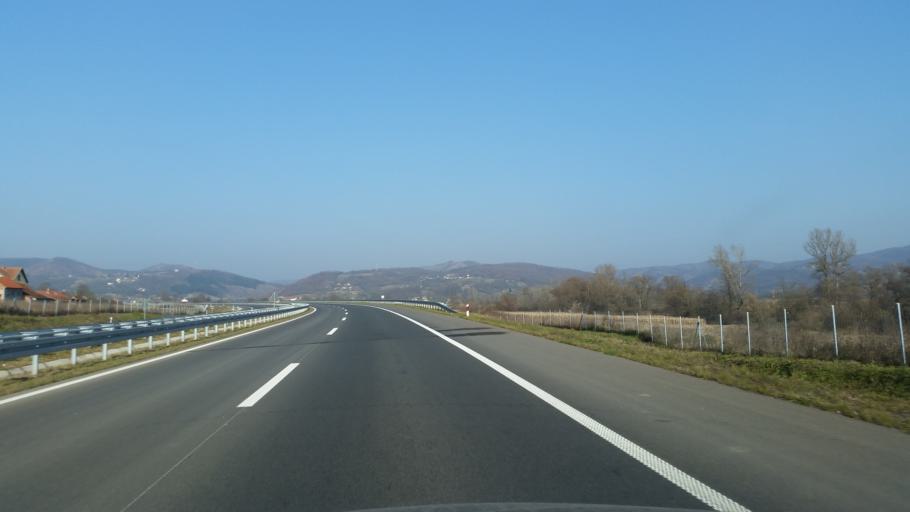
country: RS
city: Prislonica
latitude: 43.9494
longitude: 20.4008
